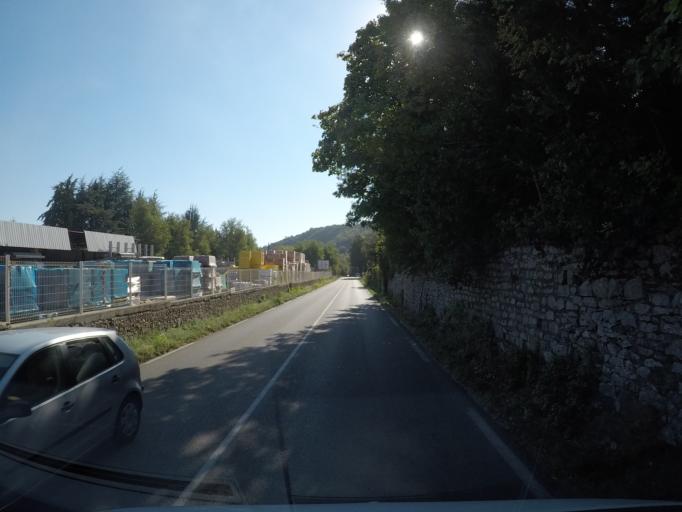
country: FR
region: Languedoc-Roussillon
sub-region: Departement du Gard
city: Anduze
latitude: 44.0403
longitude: 3.9869
